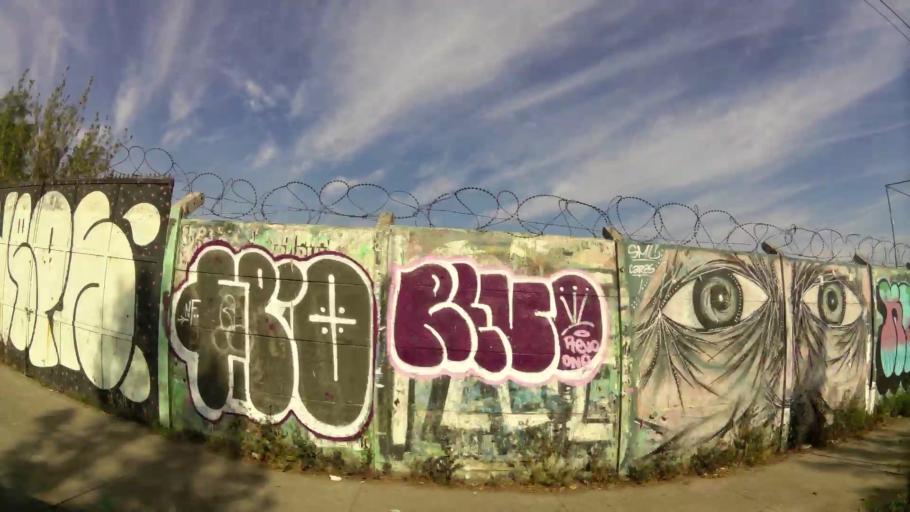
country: CL
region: Santiago Metropolitan
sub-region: Provincia de Santiago
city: Santiago
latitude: -33.5111
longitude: -70.6379
